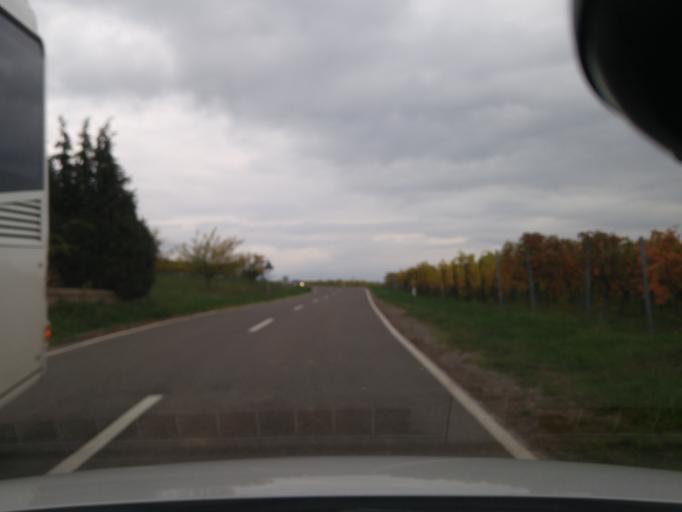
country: DE
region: Rheinland-Pfalz
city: Albersweiler
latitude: 49.2224
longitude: 8.0423
